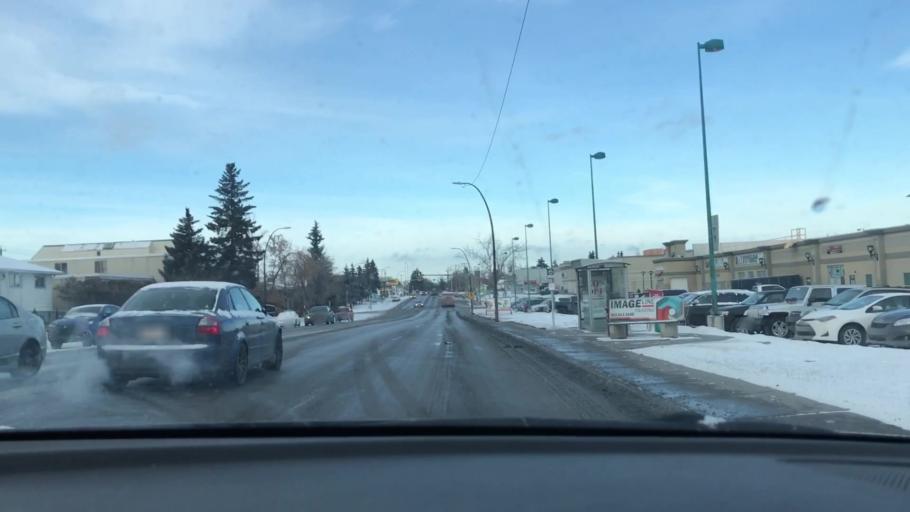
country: CA
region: Alberta
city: Calgary
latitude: 51.0417
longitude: -114.1411
